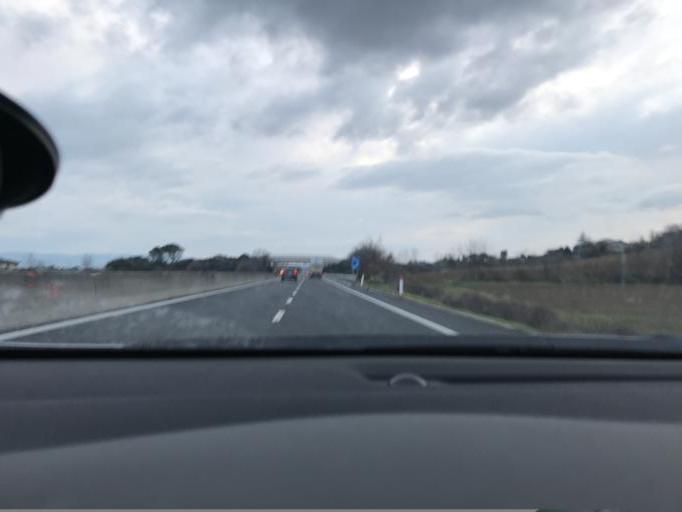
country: IT
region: Umbria
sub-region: Provincia di Perugia
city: Petrignano
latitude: 43.1259
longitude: 12.5174
